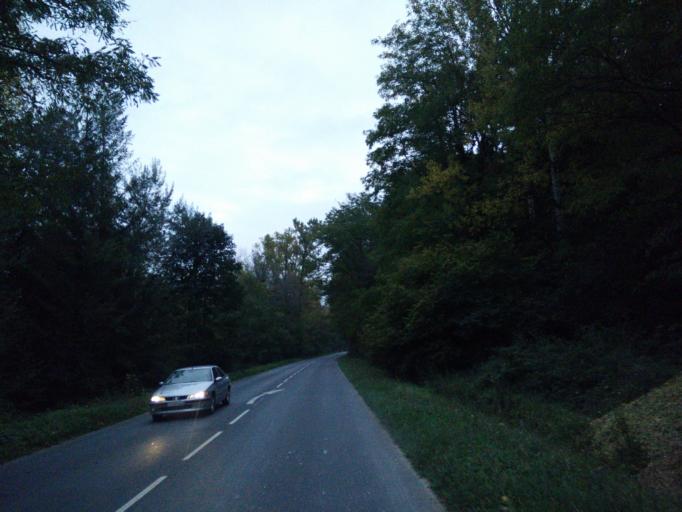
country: FR
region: Aquitaine
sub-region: Departement de la Dordogne
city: Carsac-Aillac
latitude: 44.8522
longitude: 1.2721
